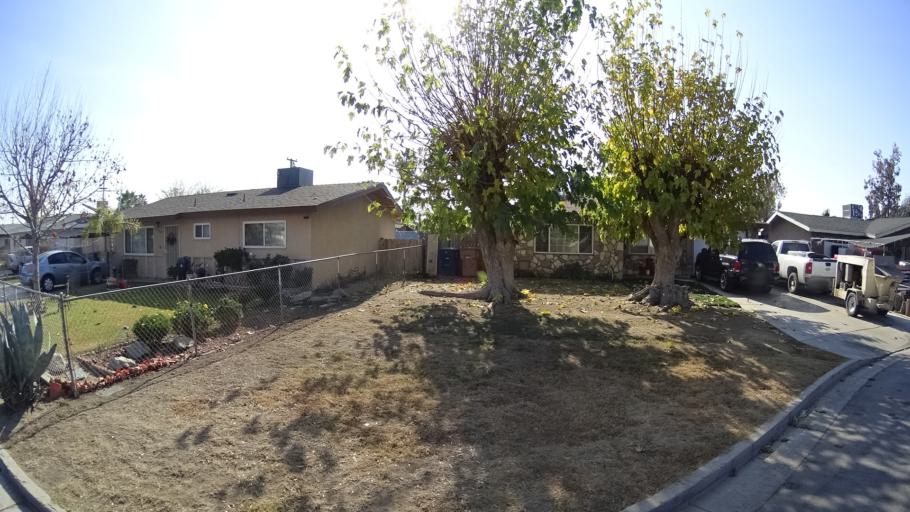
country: US
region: California
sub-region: Kern County
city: Greenfield
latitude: 35.3072
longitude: -119.0326
